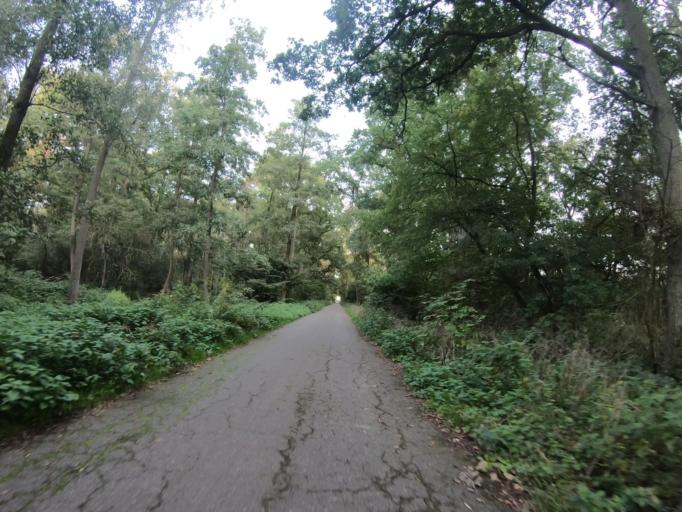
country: DE
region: Lower Saxony
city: Leiferde
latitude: 52.4341
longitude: 10.4503
